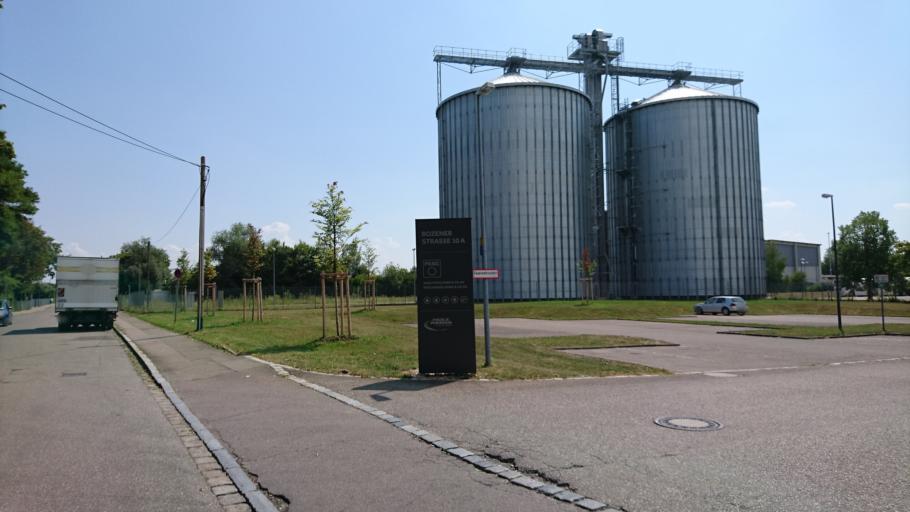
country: DE
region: Bavaria
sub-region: Swabia
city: Augsburg
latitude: 48.3847
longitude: 10.9305
